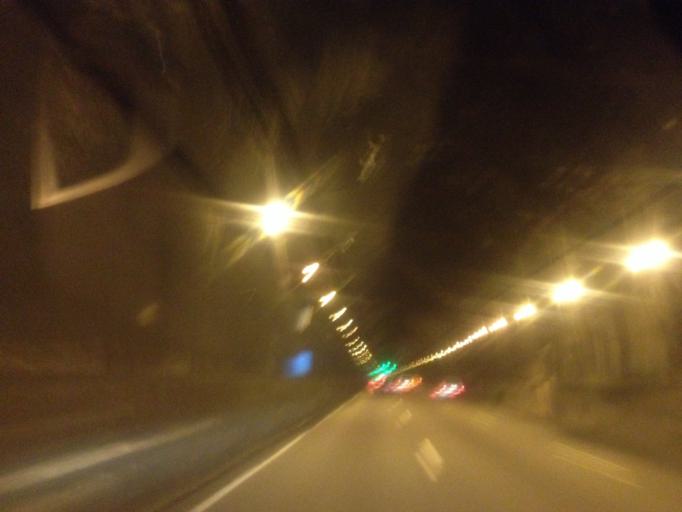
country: BR
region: Rio de Janeiro
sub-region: Rio De Janeiro
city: Rio de Janeiro
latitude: -22.9413
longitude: -43.2023
